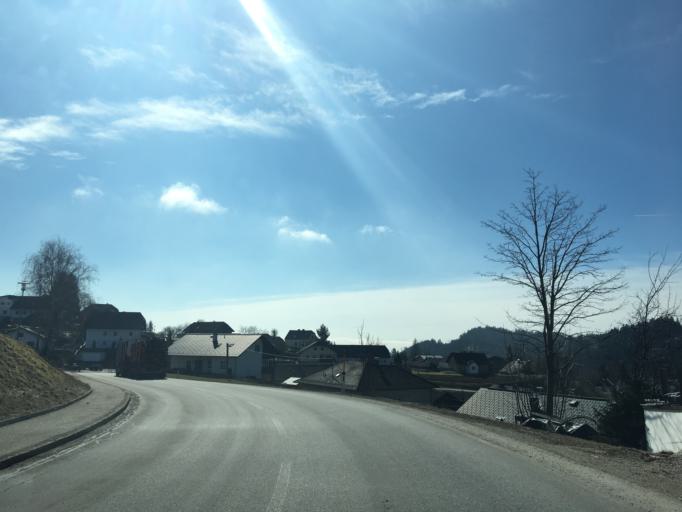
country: AT
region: Upper Austria
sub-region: Politischer Bezirk Perg
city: Sankt Georgen am Walde
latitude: 48.3621
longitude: 14.9022
